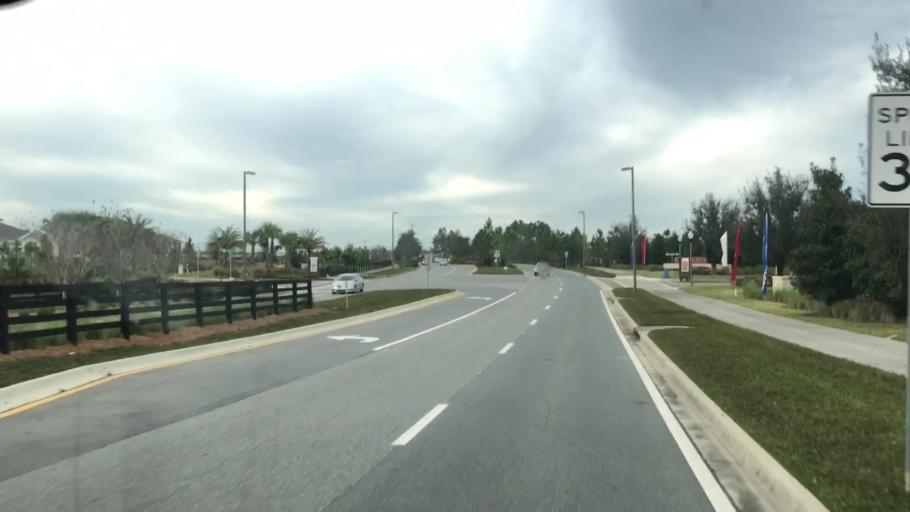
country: US
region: Florida
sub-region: Orange County
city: Lake Butler
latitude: 28.4579
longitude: -81.6239
